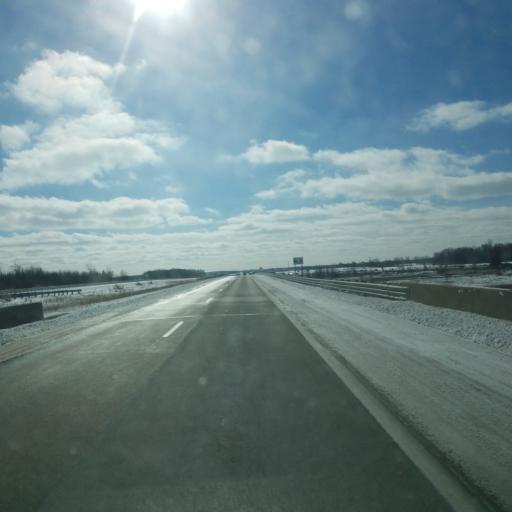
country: US
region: Michigan
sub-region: Clinton County
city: Saint Johns
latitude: 43.0053
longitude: -84.5192
